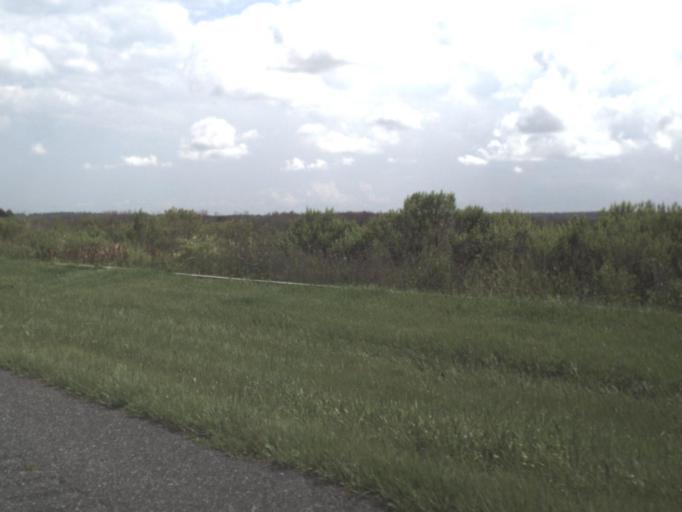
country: US
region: Florida
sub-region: Alachua County
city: Gainesville
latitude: 29.5812
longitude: -82.3370
